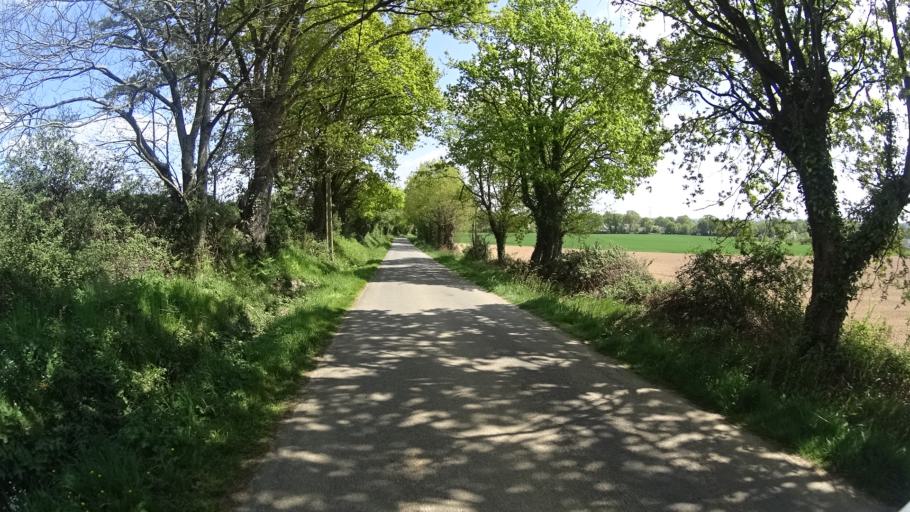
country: FR
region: Brittany
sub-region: Departement du Morbihan
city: Allaire
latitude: 47.5998
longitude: -2.1657
